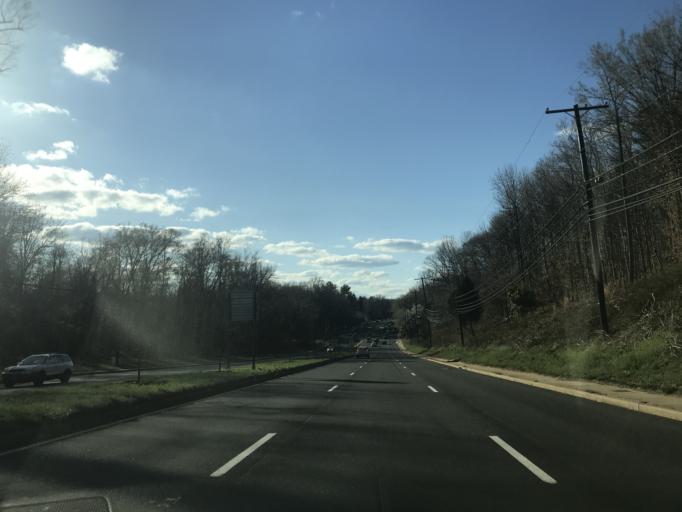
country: US
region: Maryland
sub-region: Prince George's County
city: Glenarden
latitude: 38.9193
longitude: -76.8620
